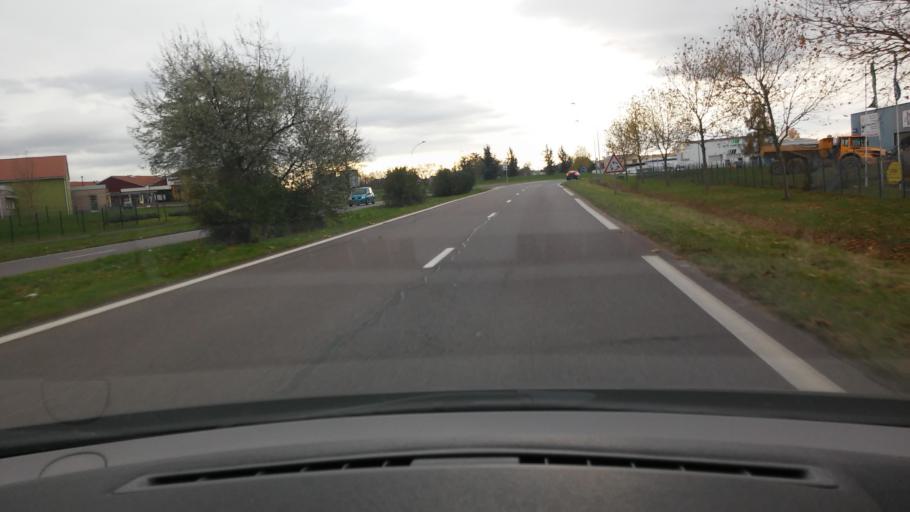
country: FR
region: Lorraine
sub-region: Departement de la Moselle
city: Ennery
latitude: 49.2215
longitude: 6.2103
